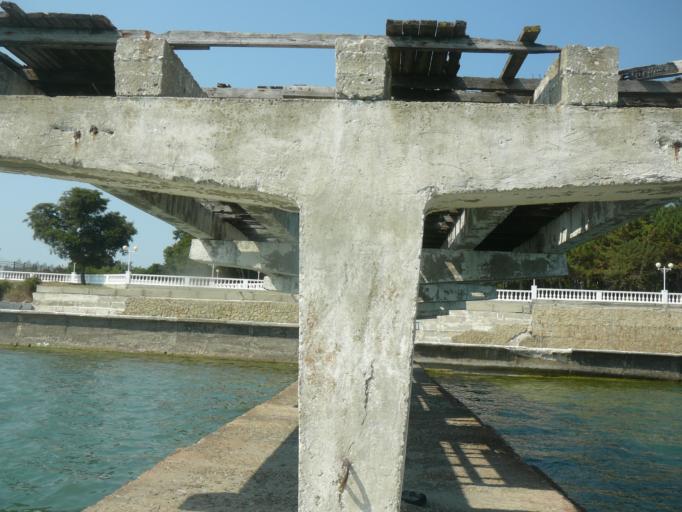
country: RU
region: Krasnodarskiy
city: Gelendzhik
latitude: 44.5850
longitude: 38.0411
